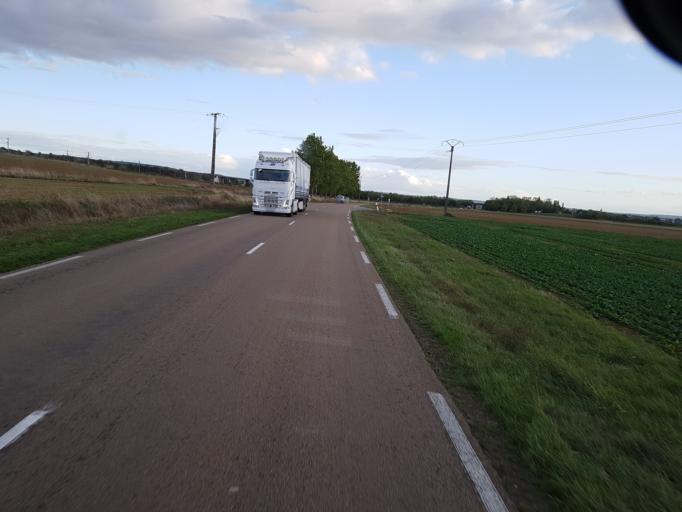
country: FR
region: Bourgogne
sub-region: Departement de l'Yonne
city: Soucy
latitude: 48.2638
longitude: 3.2813
